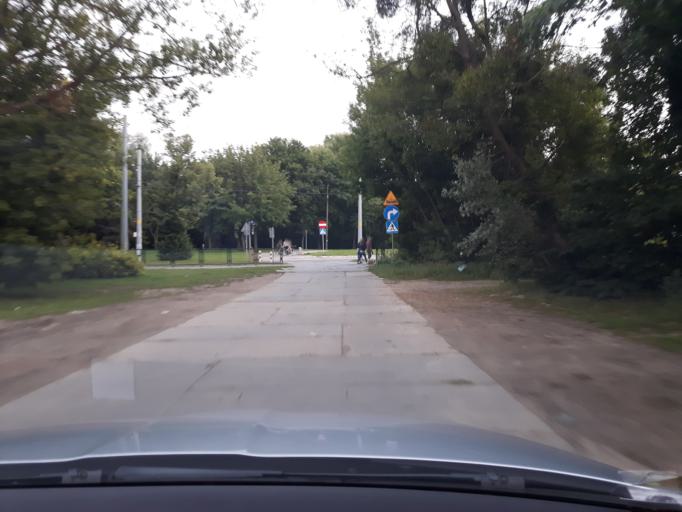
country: PL
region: Pomeranian Voivodeship
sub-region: Sopot
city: Sopot
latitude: 54.4226
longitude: 18.5903
